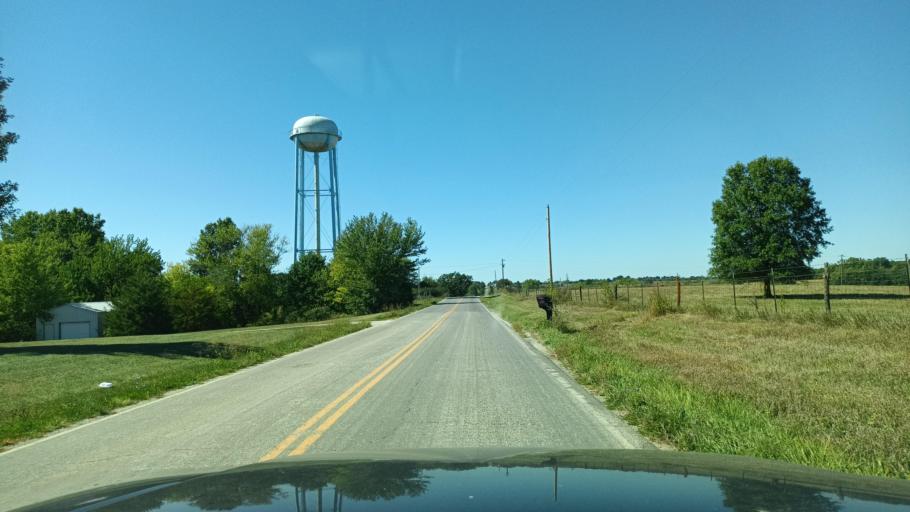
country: US
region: Missouri
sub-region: Macon County
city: La Plata
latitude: 40.0216
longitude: -92.5269
